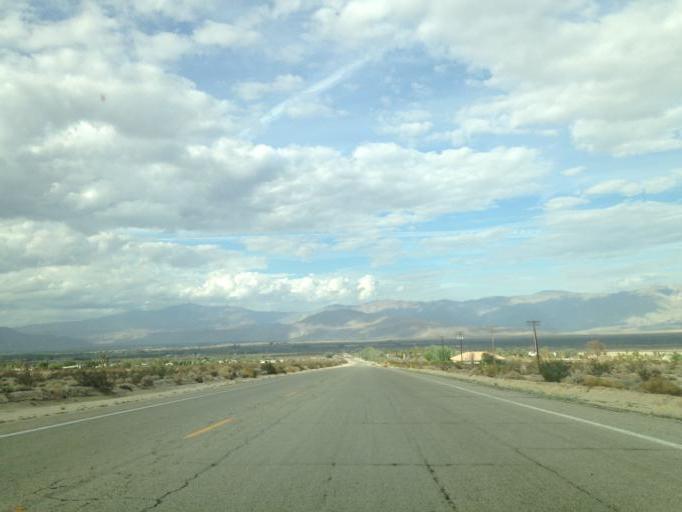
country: US
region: California
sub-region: San Diego County
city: Borrego Springs
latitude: 33.1992
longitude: -116.3302
